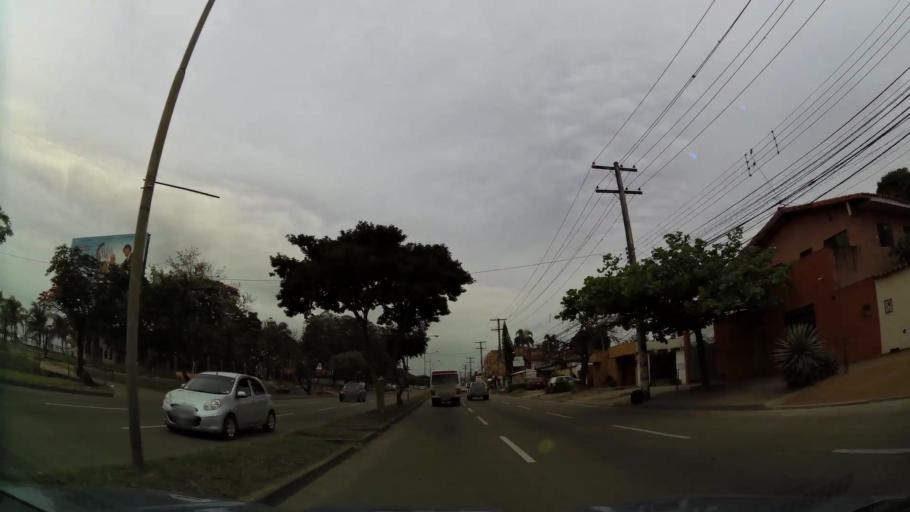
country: BO
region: Santa Cruz
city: Santa Cruz de la Sierra
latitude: -17.8028
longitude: -63.1804
